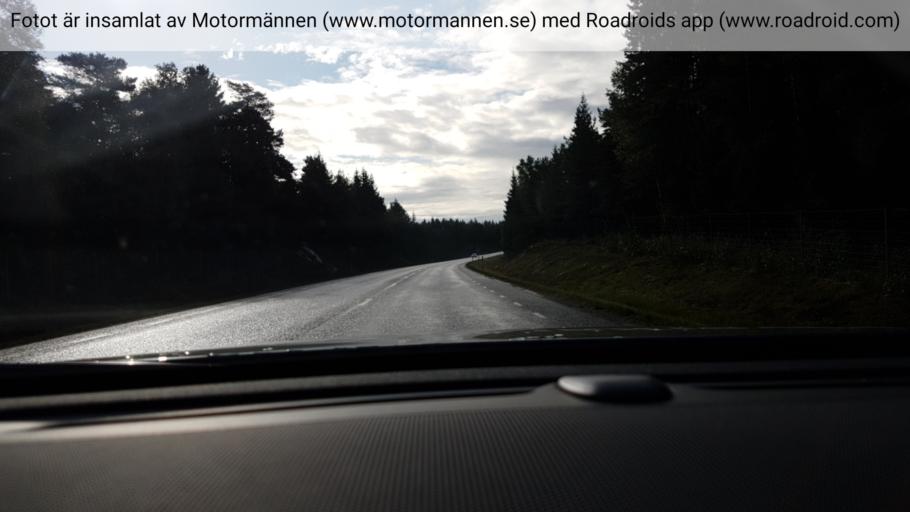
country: SE
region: Vaestra Goetaland
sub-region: Harryda Kommun
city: Hindas
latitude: 57.6659
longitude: 12.3658
